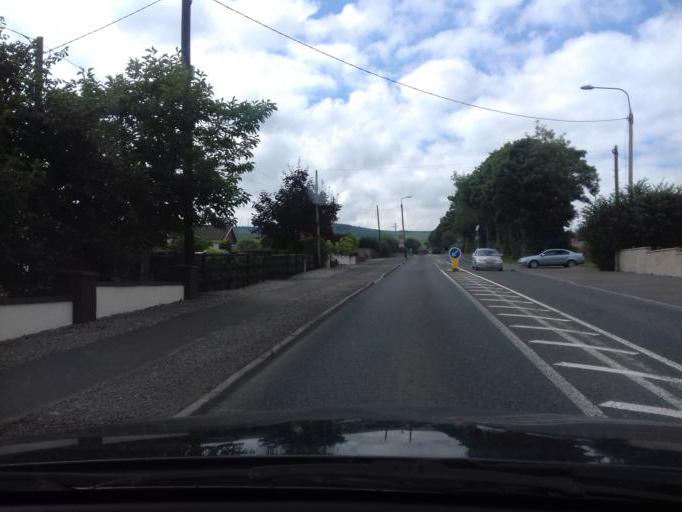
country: IE
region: Leinster
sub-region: Loch Garman
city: Bunclody
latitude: 52.6576
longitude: -6.6665
